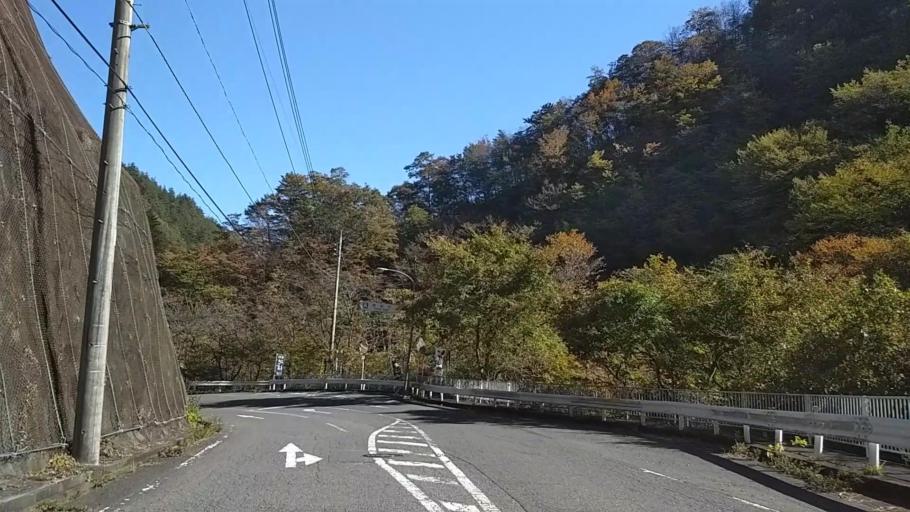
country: JP
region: Yamanashi
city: Otsuki
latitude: 35.7587
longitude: 138.9587
